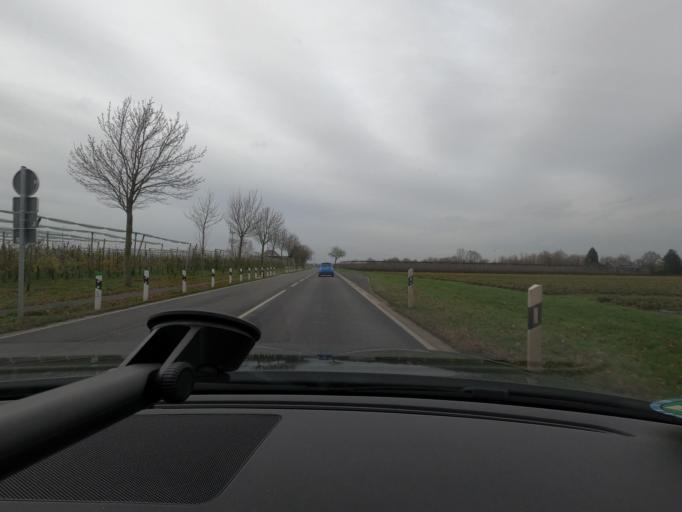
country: DE
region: North Rhine-Westphalia
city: Tonisvorst
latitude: 51.3387
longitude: 6.4950
